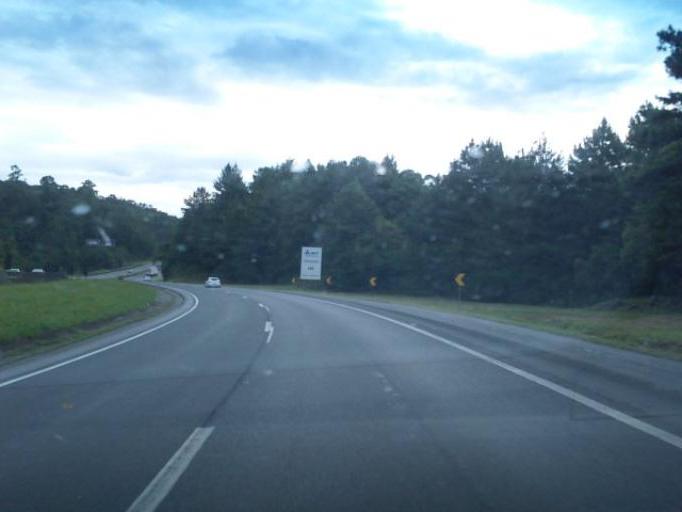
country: BR
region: Parana
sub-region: Campina Grande Do Sul
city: Campina Grande do Sul
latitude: -25.1928
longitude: -48.8881
